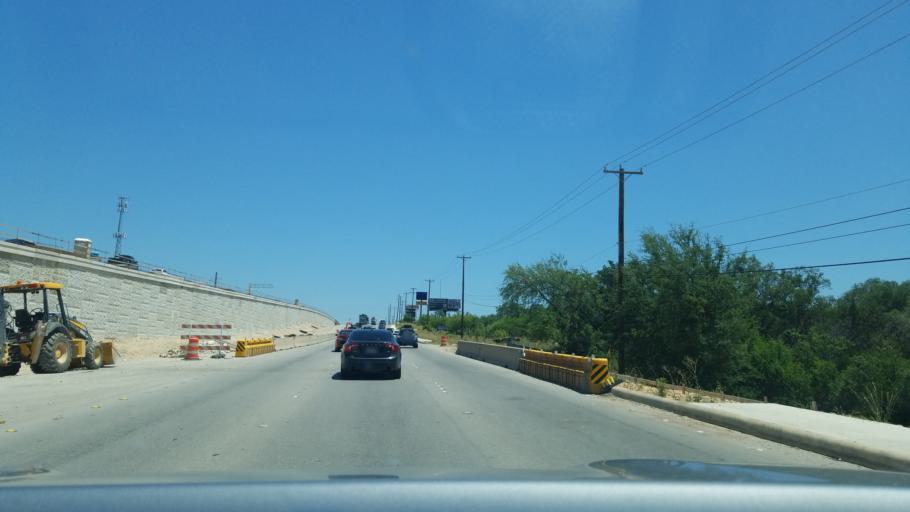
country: US
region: Texas
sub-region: Bexar County
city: Hollywood Park
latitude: 29.6263
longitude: -98.4617
